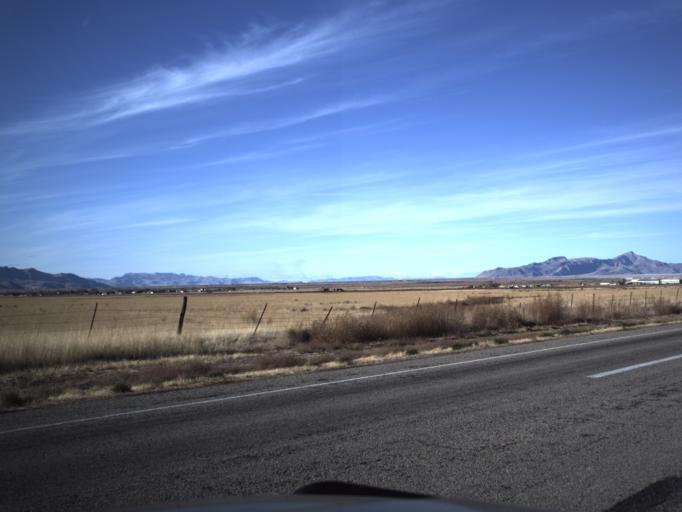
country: US
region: Utah
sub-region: Tooele County
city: Erda
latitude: 40.5871
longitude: -112.3701
